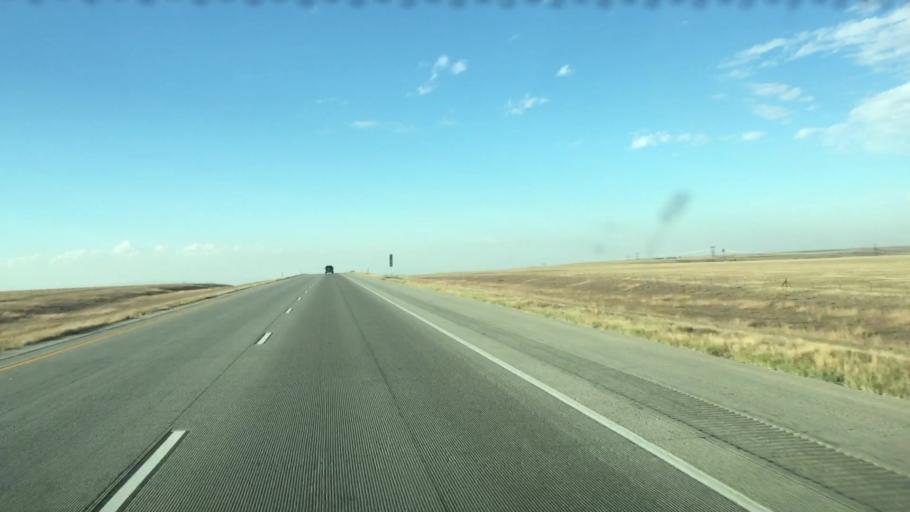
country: US
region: Colorado
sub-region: Lincoln County
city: Limon
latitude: 39.3892
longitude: -103.8887
